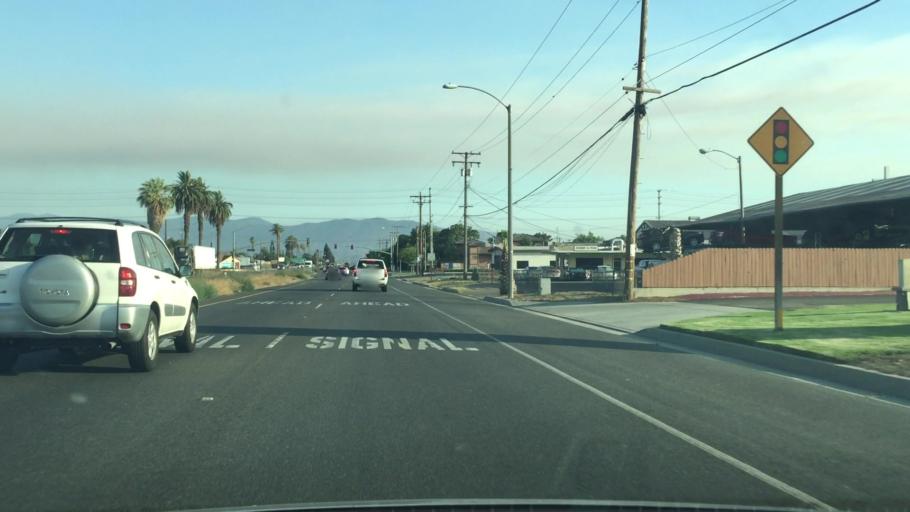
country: US
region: California
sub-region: San Bernardino County
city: Chino
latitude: 33.9995
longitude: -117.6509
